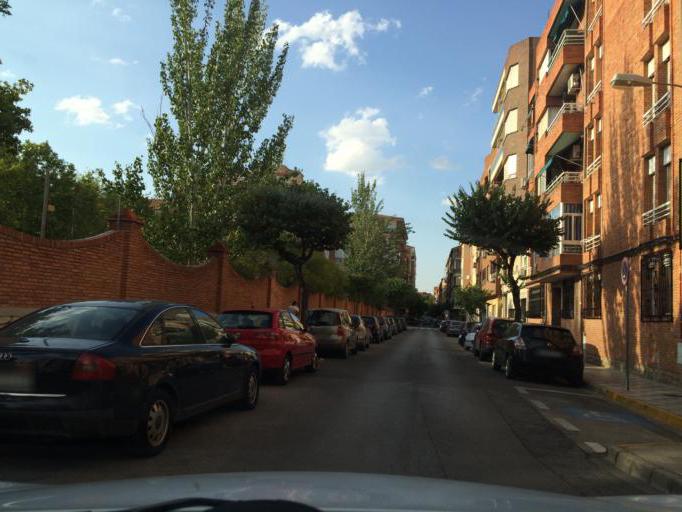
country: ES
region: Castille-La Mancha
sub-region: Provincia de Albacete
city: Albacete
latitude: 38.9920
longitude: -1.8652
